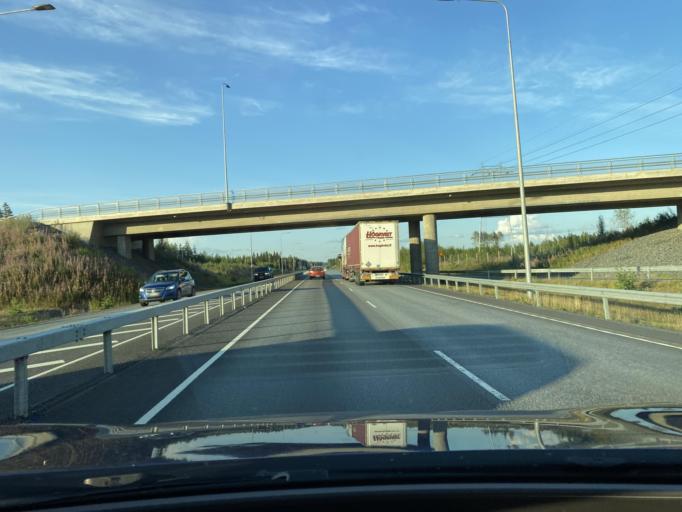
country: FI
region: Southern Ostrobothnia
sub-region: Seinaejoki
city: Seinaejoki
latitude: 62.7241
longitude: 22.8760
